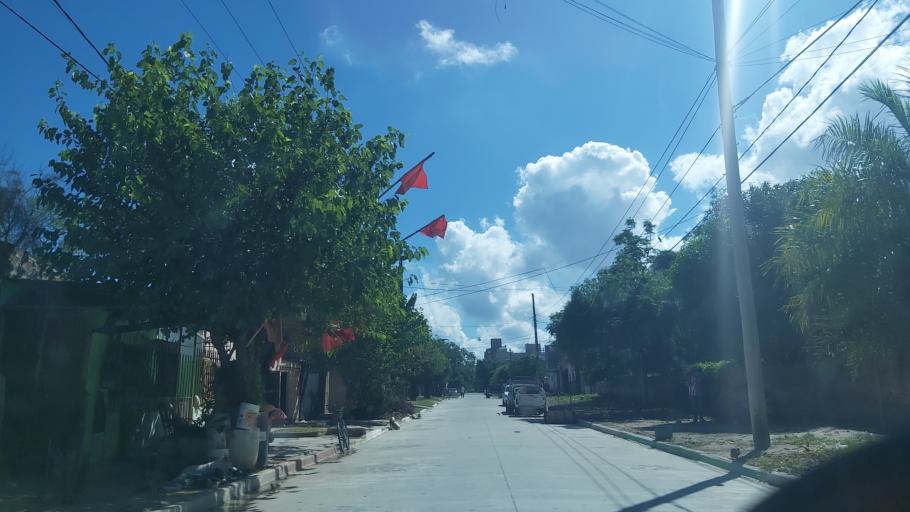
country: AR
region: Corrientes
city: Corrientes
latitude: -27.4789
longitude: -58.8501
